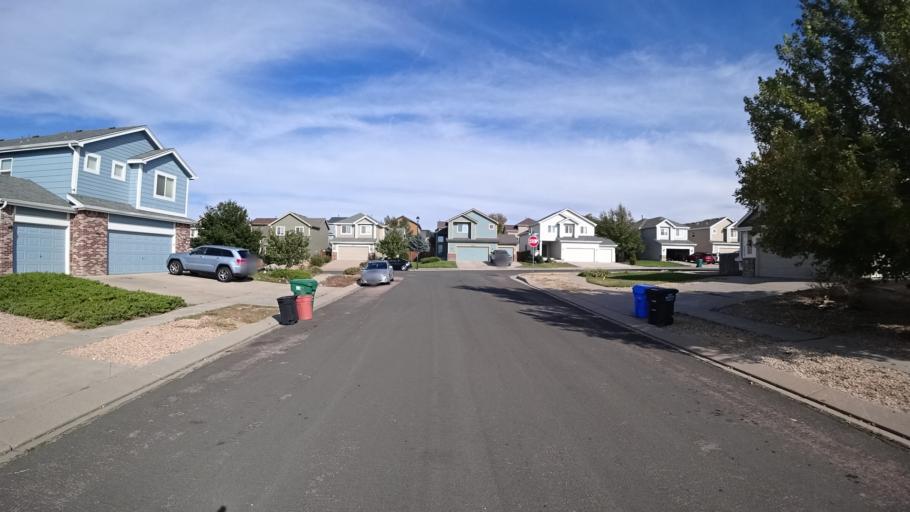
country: US
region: Colorado
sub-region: El Paso County
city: Cimarron Hills
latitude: 38.9072
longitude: -104.6903
